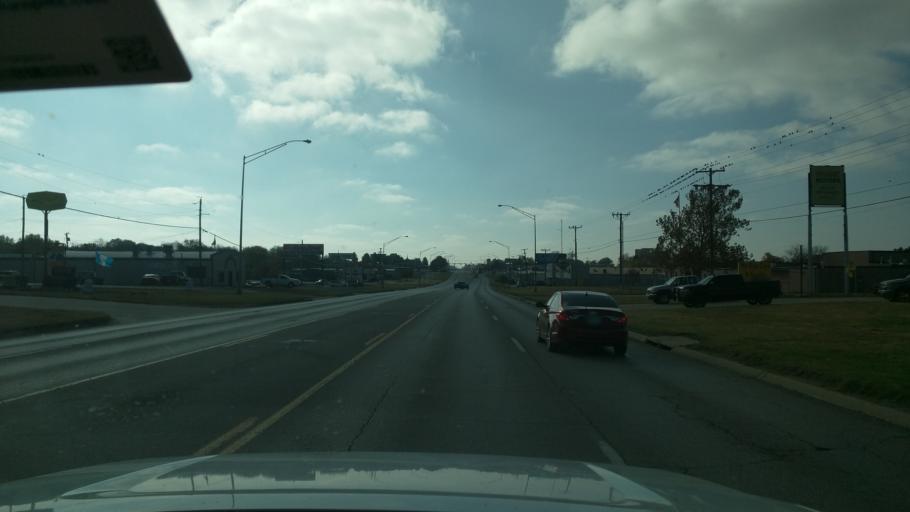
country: US
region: Oklahoma
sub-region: Washington County
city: Dewey
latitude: 36.7620
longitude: -95.9355
